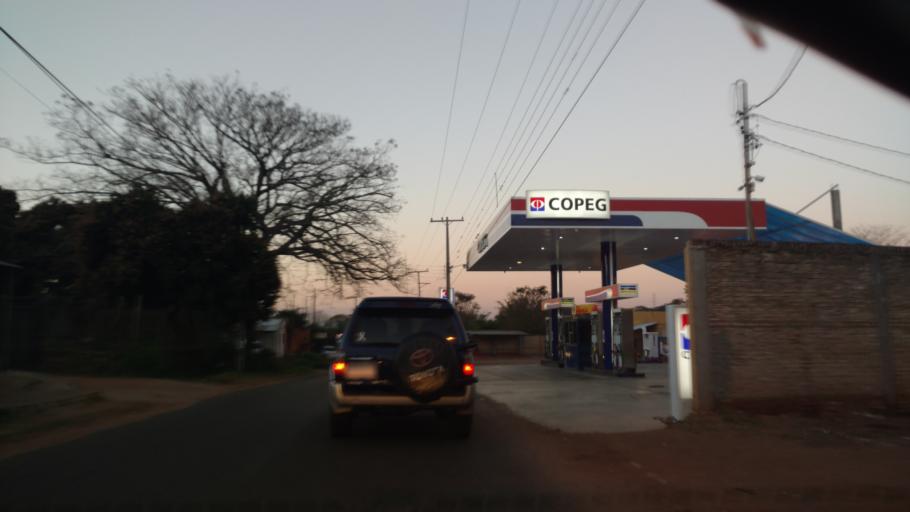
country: PY
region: Central
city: Guarambare
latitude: -25.4752
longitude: -57.4132
